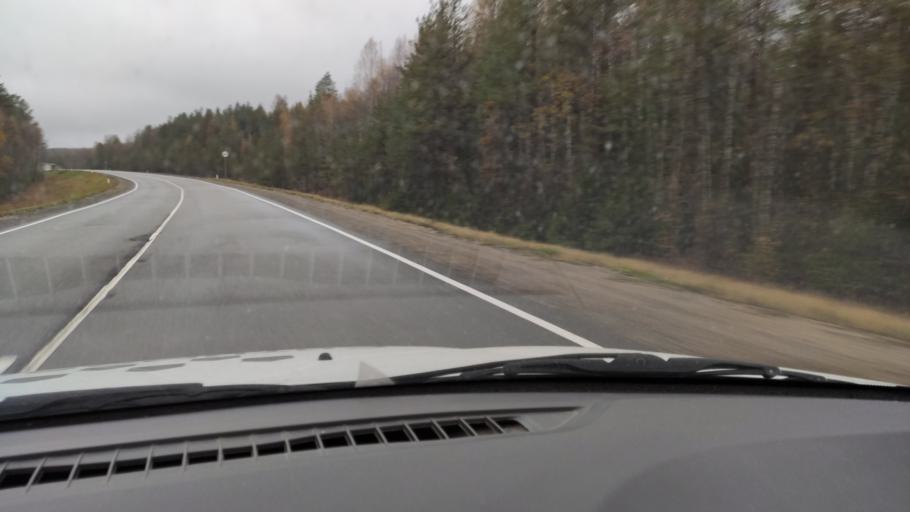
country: RU
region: Kirov
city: Chernaya Kholunitsa
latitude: 58.8208
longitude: 51.8093
